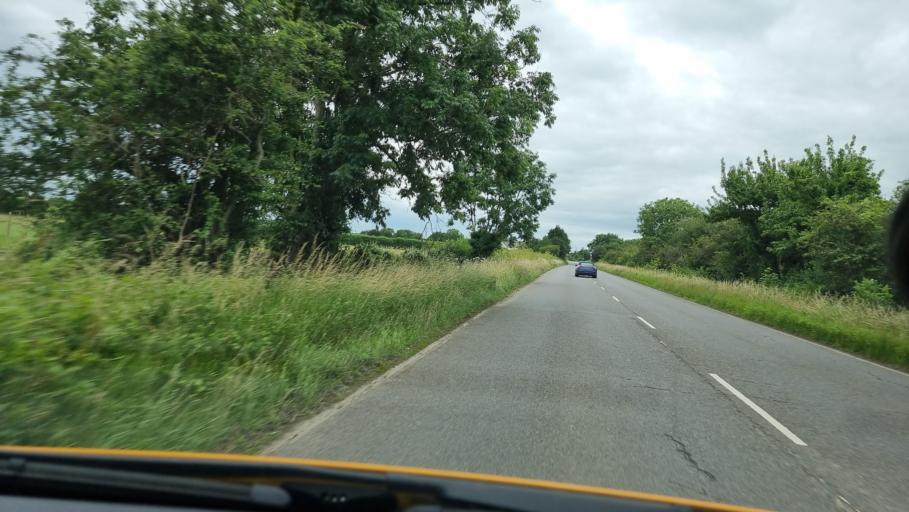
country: GB
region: England
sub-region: Oxfordshire
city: Woodstock
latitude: 51.8659
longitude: -1.3260
